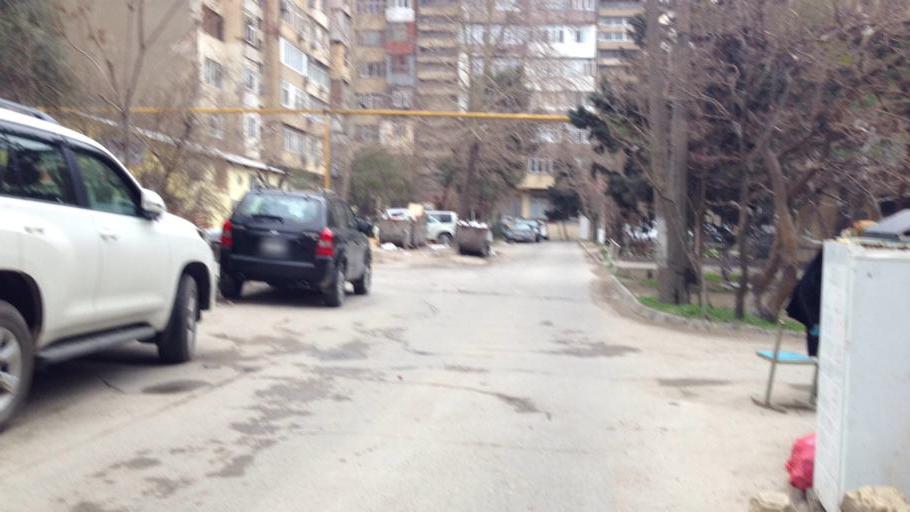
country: AZ
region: Baki
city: Baku
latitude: 40.4014
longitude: 49.8614
